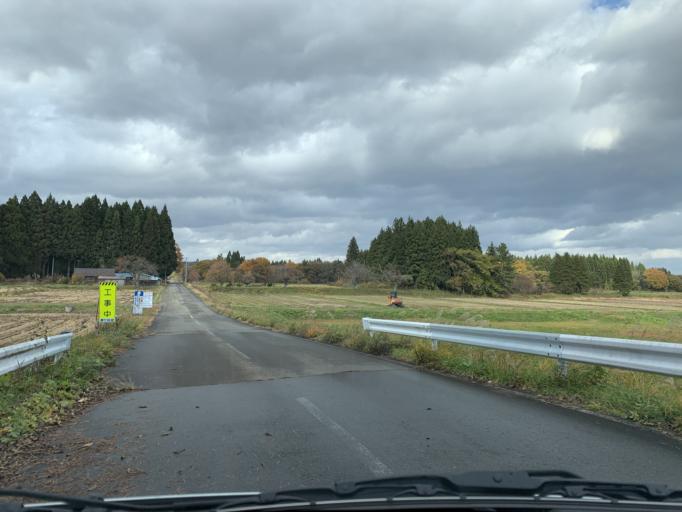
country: JP
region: Iwate
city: Mizusawa
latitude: 39.1128
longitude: 140.9736
